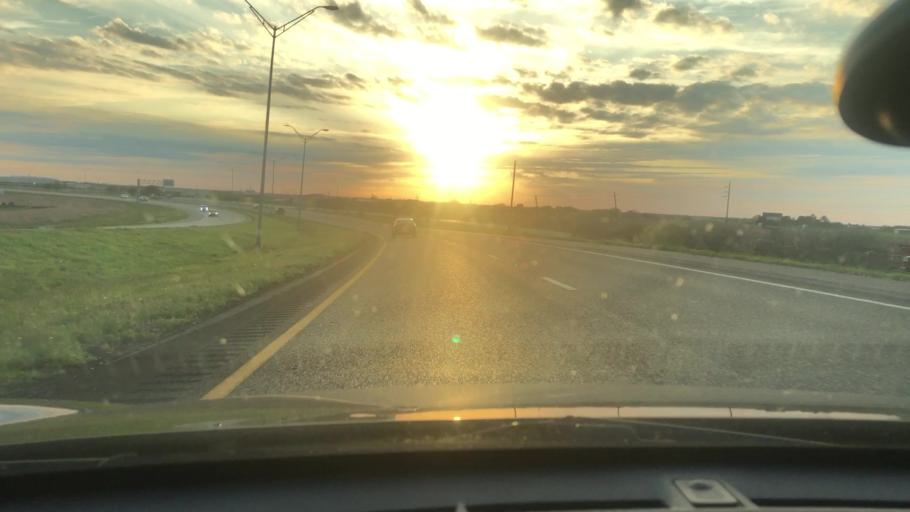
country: US
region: Texas
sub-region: Wharton County
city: El Campo
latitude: 29.1740
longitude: -96.3057
